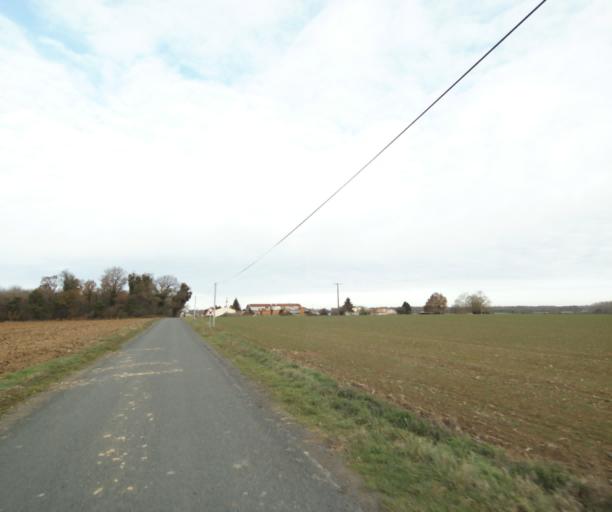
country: FR
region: Poitou-Charentes
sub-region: Departement de la Charente-Maritime
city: Corme-Royal
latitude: 45.7842
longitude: -0.8172
